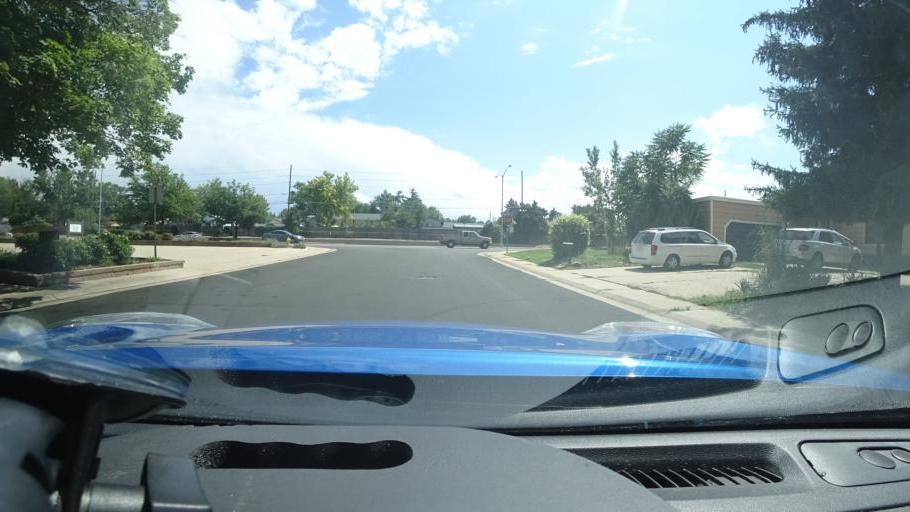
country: US
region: Colorado
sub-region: Adams County
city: Aurora
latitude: 39.7116
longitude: -104.8386
